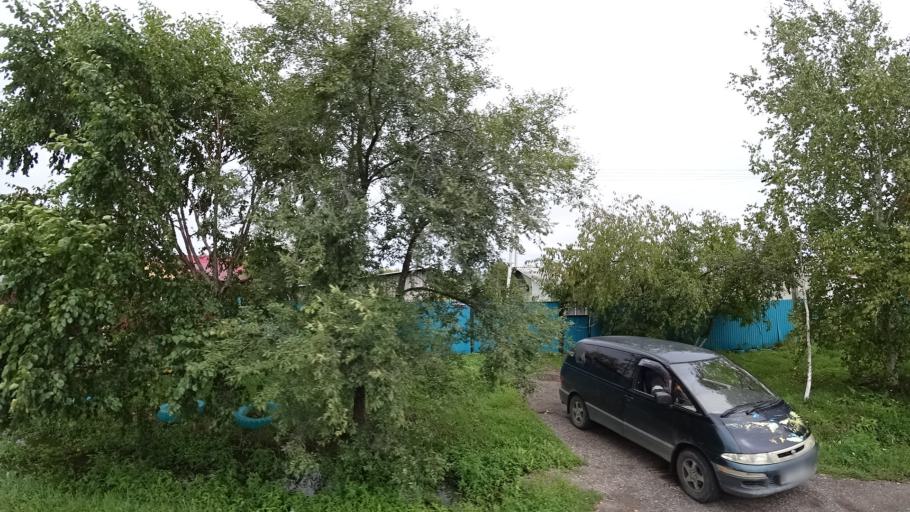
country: RU
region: Primorskiy
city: Monastyrishche
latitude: 44.2012
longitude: 132.4562
